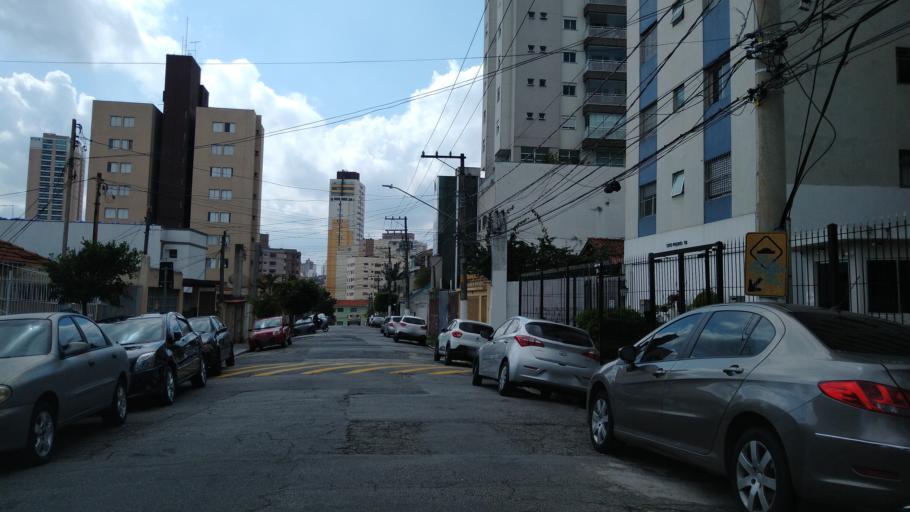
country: BR
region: Sao Paulo
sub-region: Sao Paulo
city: Sao Paulo
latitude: -23.4898
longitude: -46.6029
